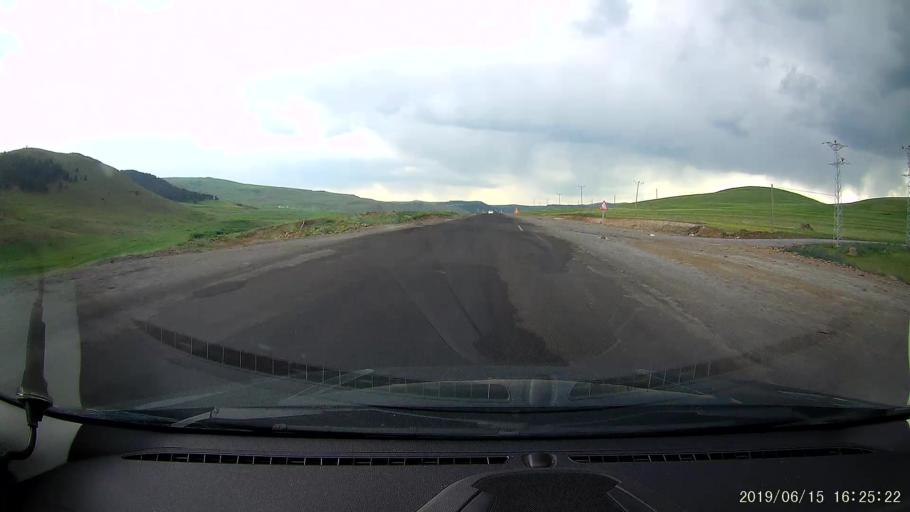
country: TR
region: Ardahan
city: Hanak
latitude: 41.1546
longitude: 42.8704
